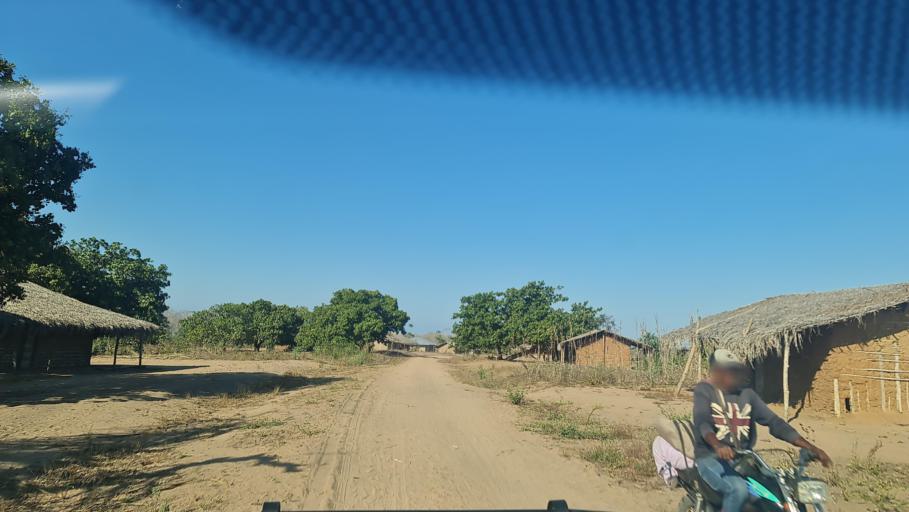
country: MZ
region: Nampula
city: Nacala
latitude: -13.9417
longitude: 40.4848
